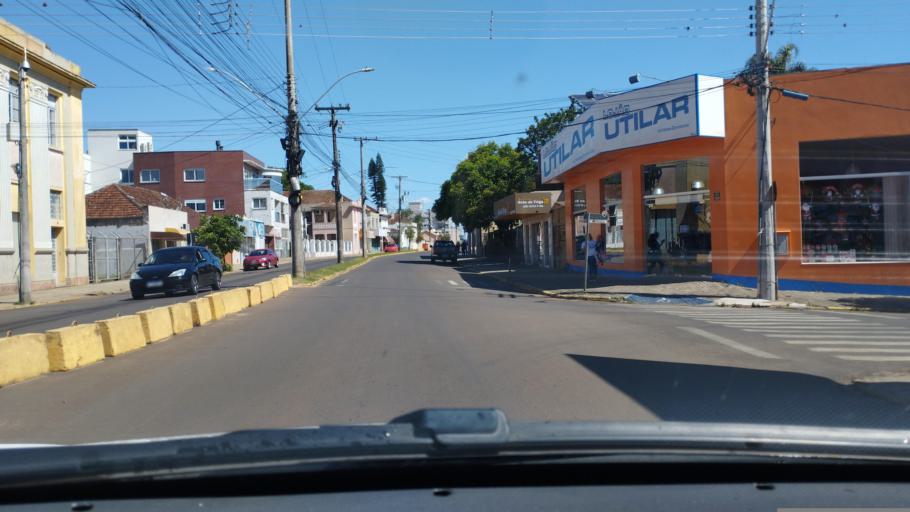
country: BR
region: Rio Grande do Sul
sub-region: Tupancireta
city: Tupancireta
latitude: -29.0823
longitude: -53.8363
